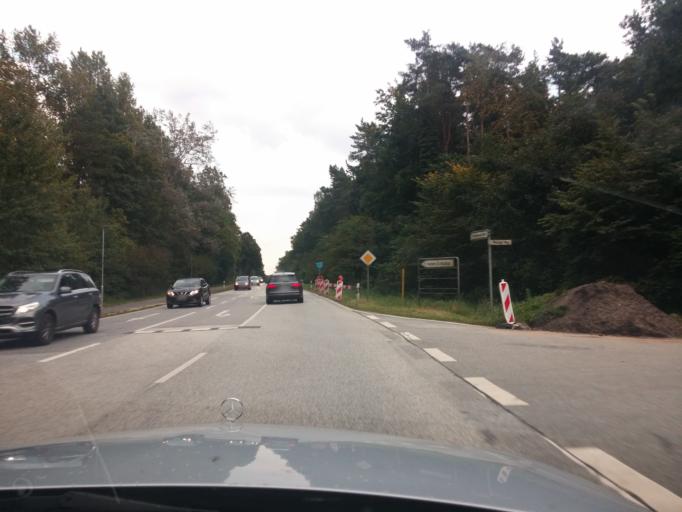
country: DE
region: Schleswig-Holstein
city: Ratekau
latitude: 53.8950
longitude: 10.7516
